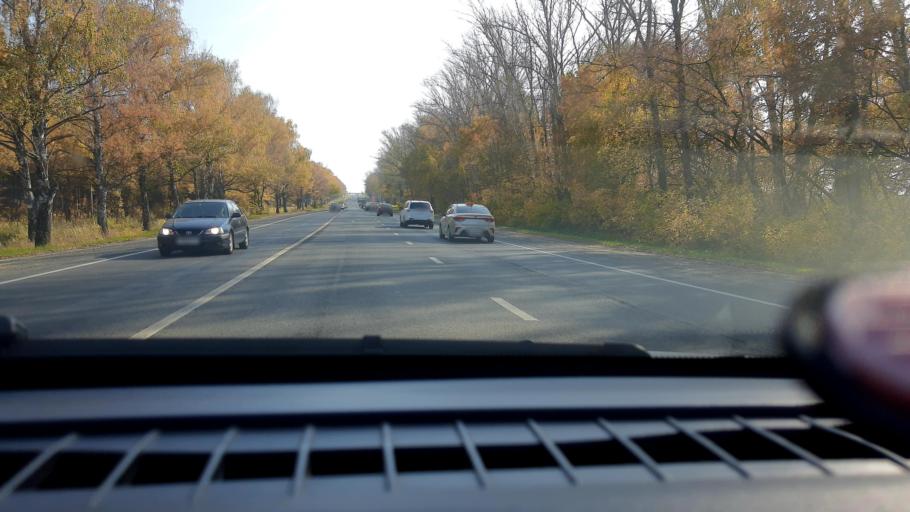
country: RU
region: Nizjnij Novgorod
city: Kstovo
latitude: 56.1398
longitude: 44.2310
